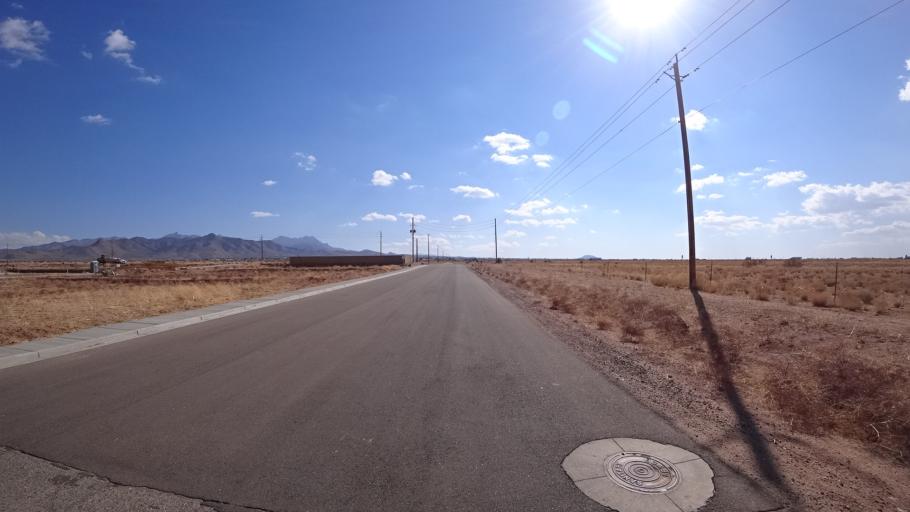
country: US
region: Arizona
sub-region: Mohave County
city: New Kingman-Butler
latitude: 35.2189
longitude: -113.9762
